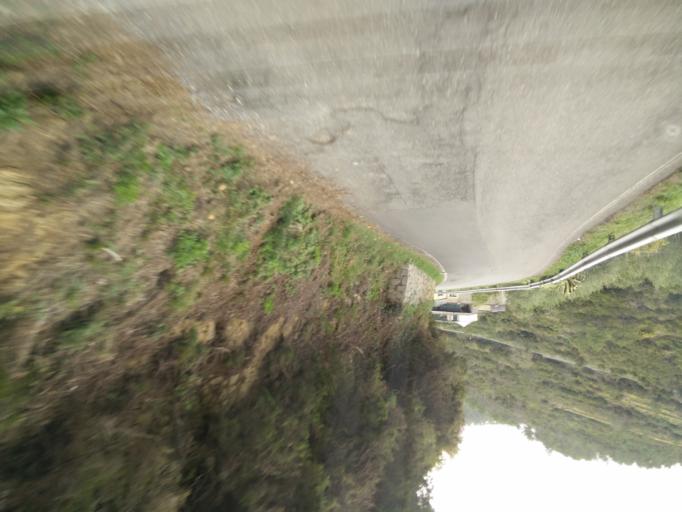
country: IT
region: Liguria
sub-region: Provincia di La Spezia
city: Riomaggiore
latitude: 44.1142
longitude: 9.7377
